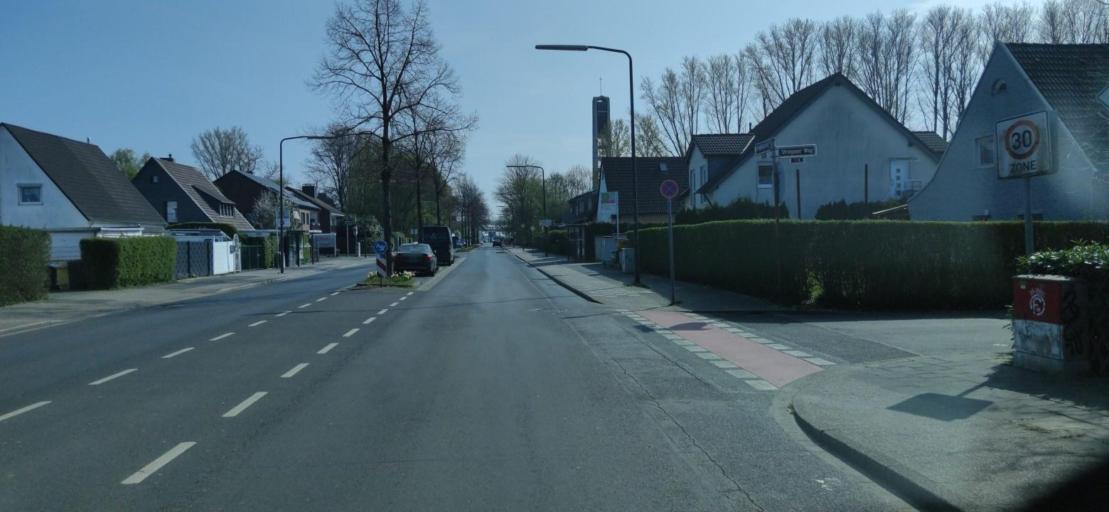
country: DE
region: North Rhine-Westphalia
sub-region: Regierungsbezirk Dusseldorf
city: Erkrath
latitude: 51.2131
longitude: 6.8534
